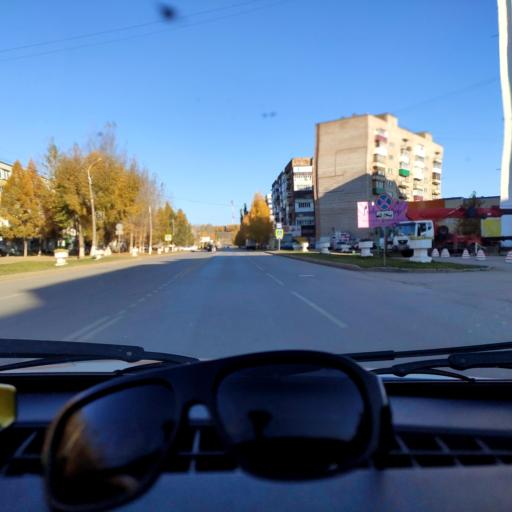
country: RU
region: Bashkortostan
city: Blagoveshchensk
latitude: 55.0495
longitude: 55.9551
